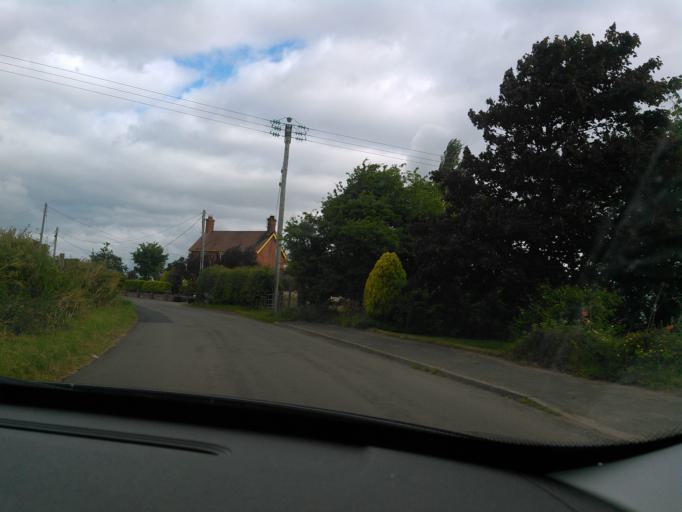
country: GB
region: England
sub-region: Shropshire
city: Wem
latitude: 52.8617
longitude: -2.7321
